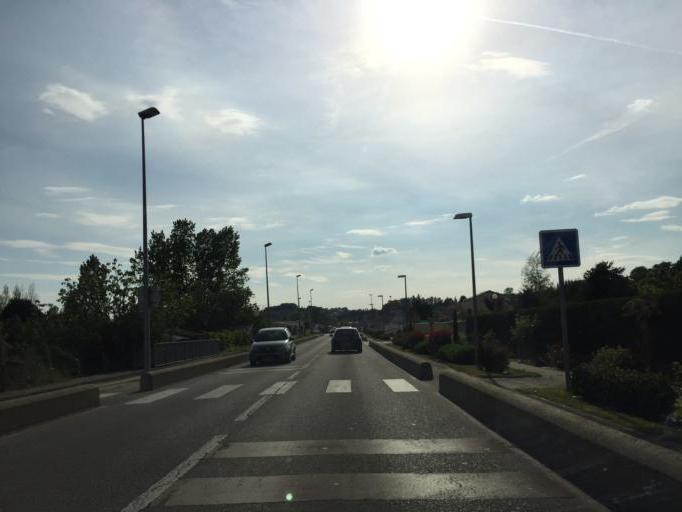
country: FR
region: Rhone-Alpes
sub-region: Departement de la Drome
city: Clerieux
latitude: 45.1199
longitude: 4.9779
